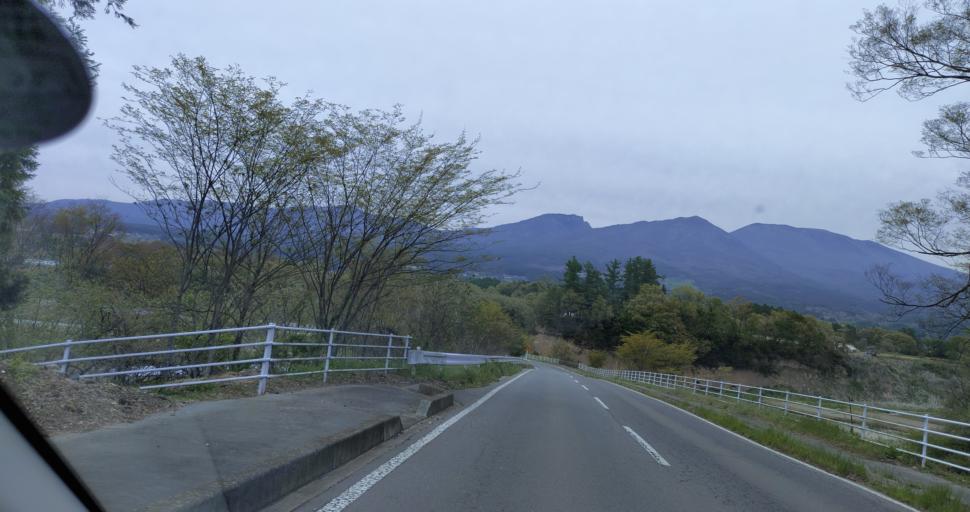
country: JP
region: Nagano
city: Komoro
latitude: 36.3224
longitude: 138.4927
